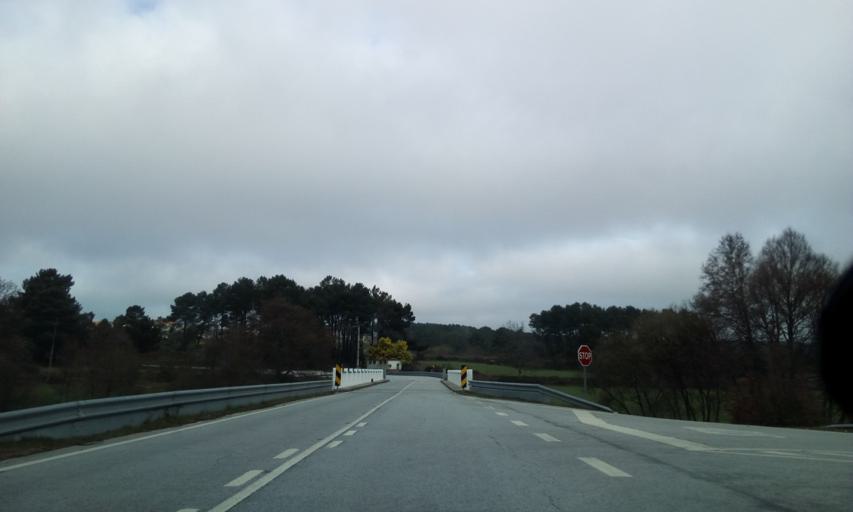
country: PT
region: Guarda
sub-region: Fornos de Algodres
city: Fornos de Algodres
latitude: 40.7180
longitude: -7.4879
